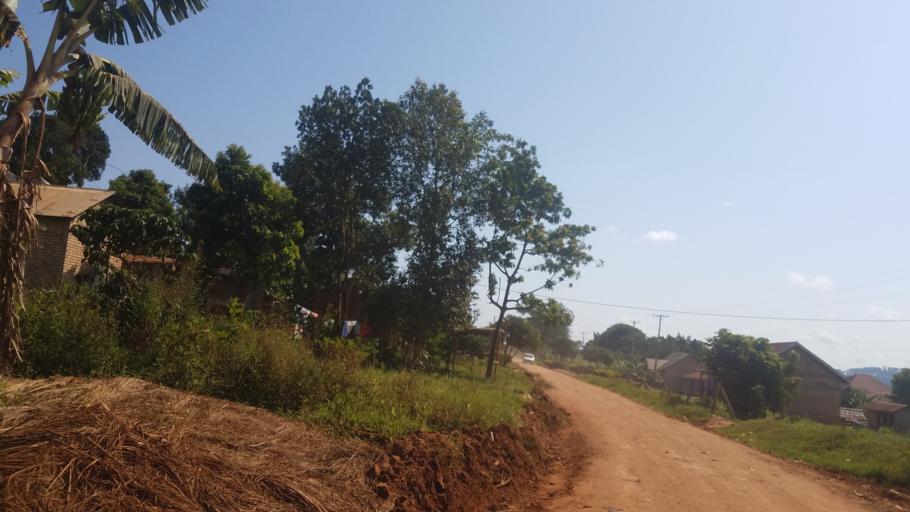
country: UG
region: Central Region
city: Masaka
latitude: -0.3343
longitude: 31.7090
